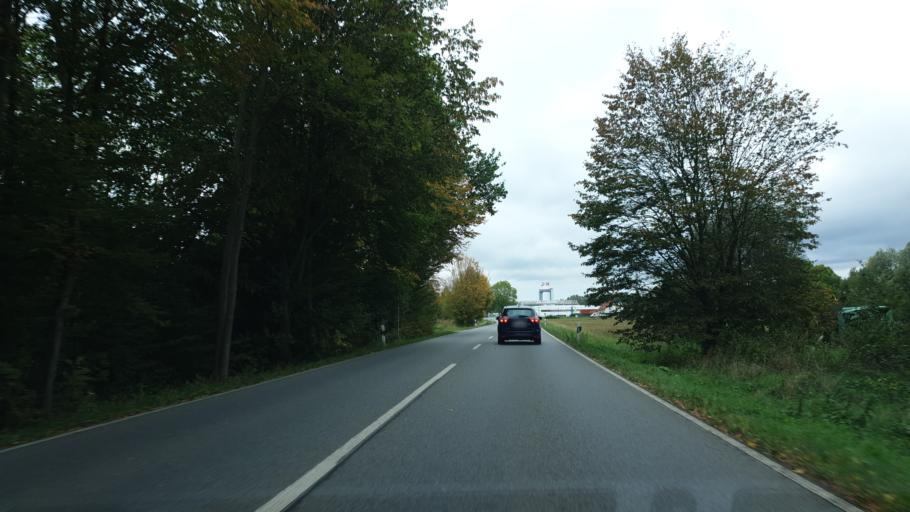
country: DE
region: Saxony
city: Glauchau
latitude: 50.8208
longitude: 12.5656
